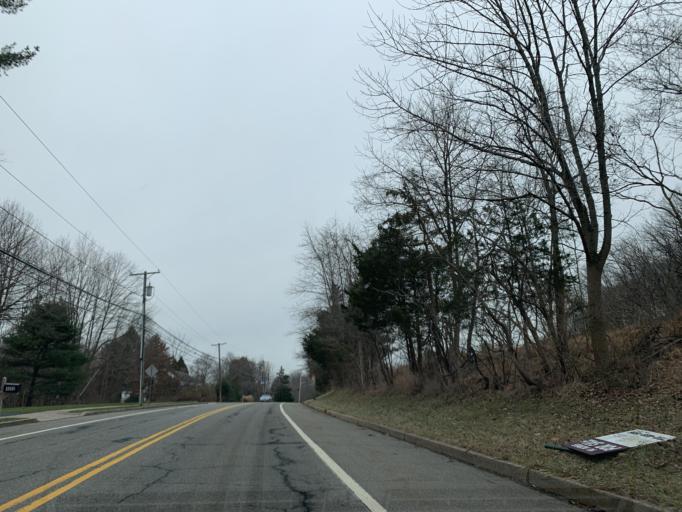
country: US
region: New Jersey
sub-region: Somerset County
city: Green Knoll
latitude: 40.6190
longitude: -74.5867
